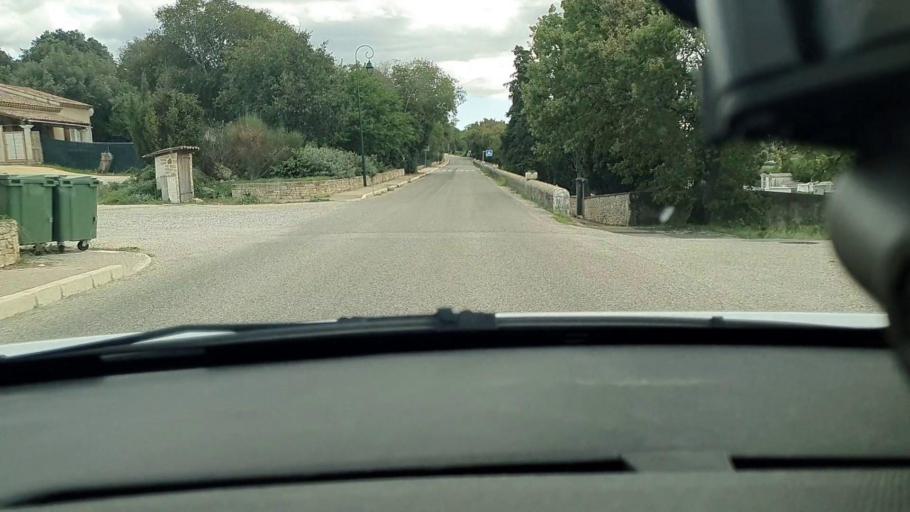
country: FR
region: Languedoc-Roussillon
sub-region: Departement du Gard
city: Salindres
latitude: 44.1665
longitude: 4.2388
